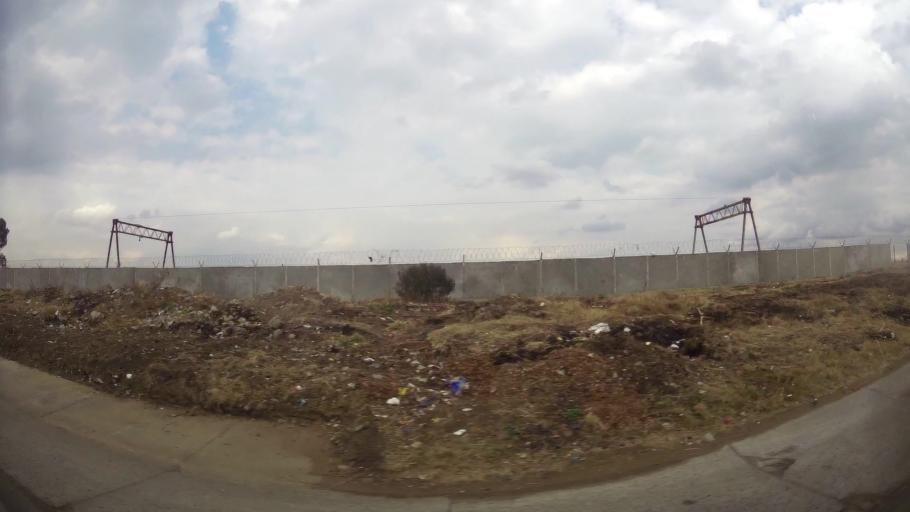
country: ZA
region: Orange Free State
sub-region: Fezile Dabi District Municipality
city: Sasolburg
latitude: -26.8612
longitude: 27.8590
